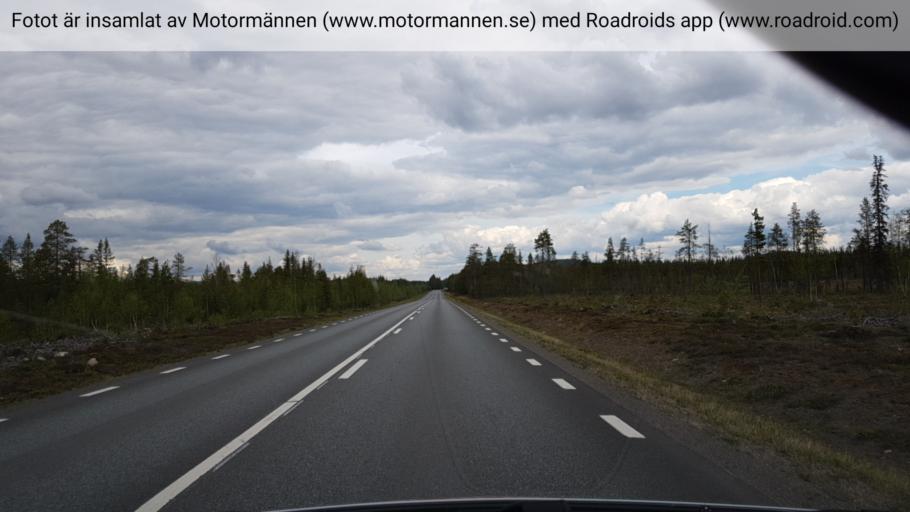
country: SE
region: Norrbotten
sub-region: Arvidsjaurs Kommun
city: Arvidsjaur
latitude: 65.5007
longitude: 19.2958
